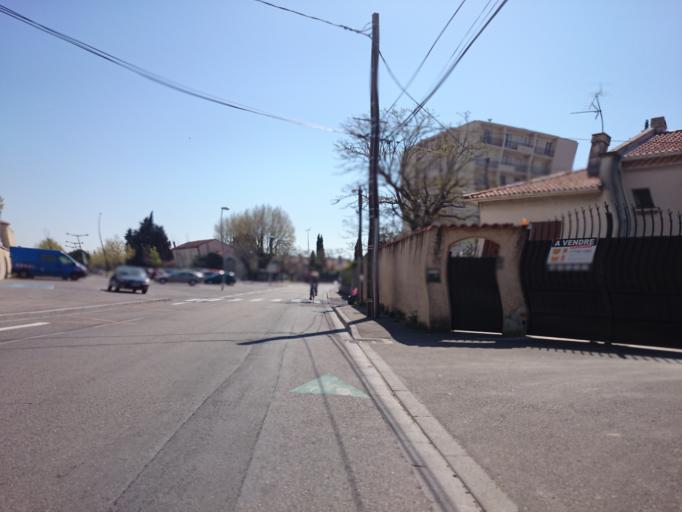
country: FR
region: Provence-Alpes-Cote d'Azur
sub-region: Departement du Vaucluse
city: Avignon
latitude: 43.9299
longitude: 4.7985
